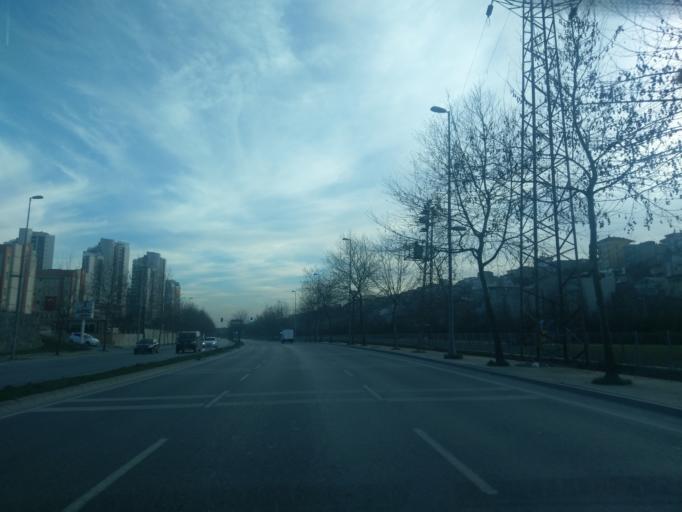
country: TR
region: Istanbul
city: Basaksehir
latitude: 41.0542
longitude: 28.7573
